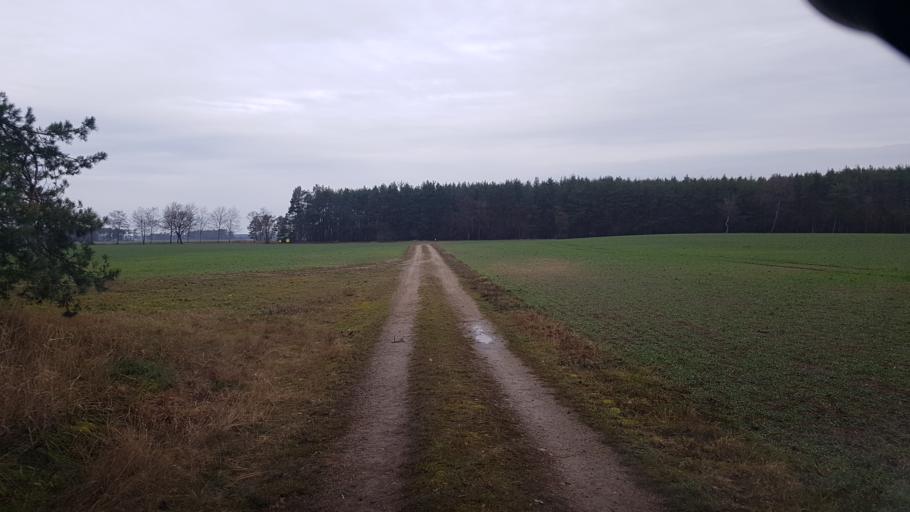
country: DE
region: Brandenburg
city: Bad Liebenwerda
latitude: 51.5361
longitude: 13.3336
